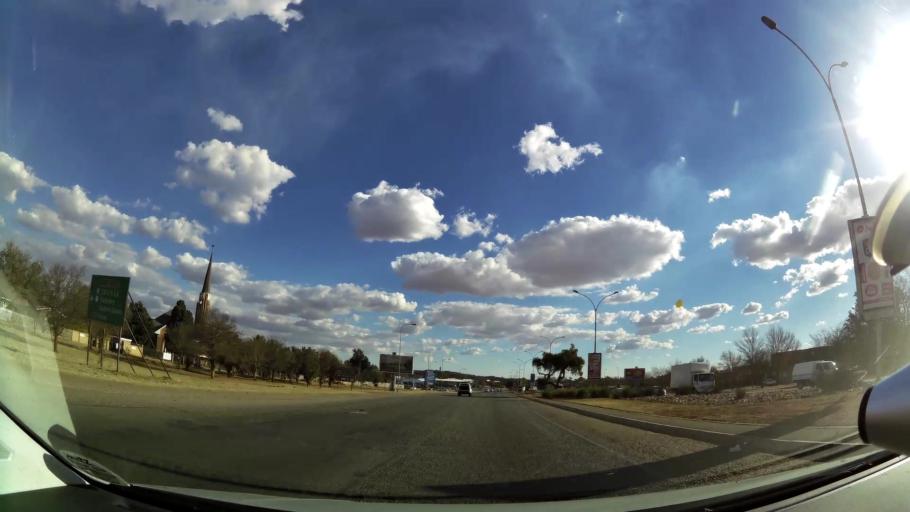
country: ZA
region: North-West
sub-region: Dr Kenneth Kaunda District Municipality
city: Klerksdorp
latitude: -26.8579
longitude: 26.6735
